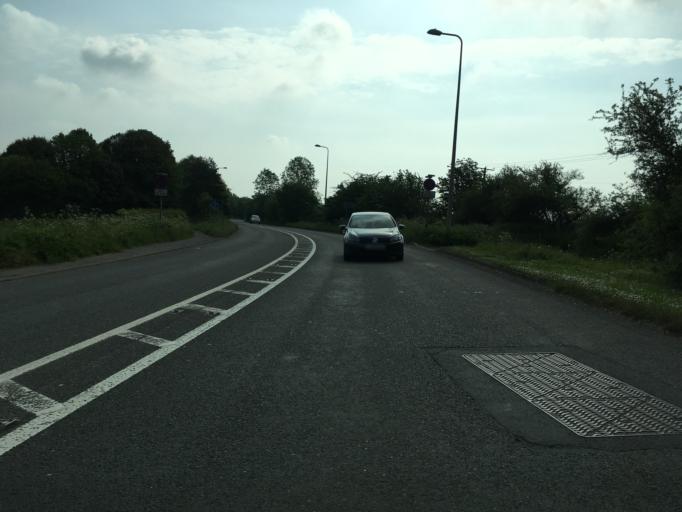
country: GB
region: England
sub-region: North Somerset
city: Long Ashton
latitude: 51.4210
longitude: -2.6978
